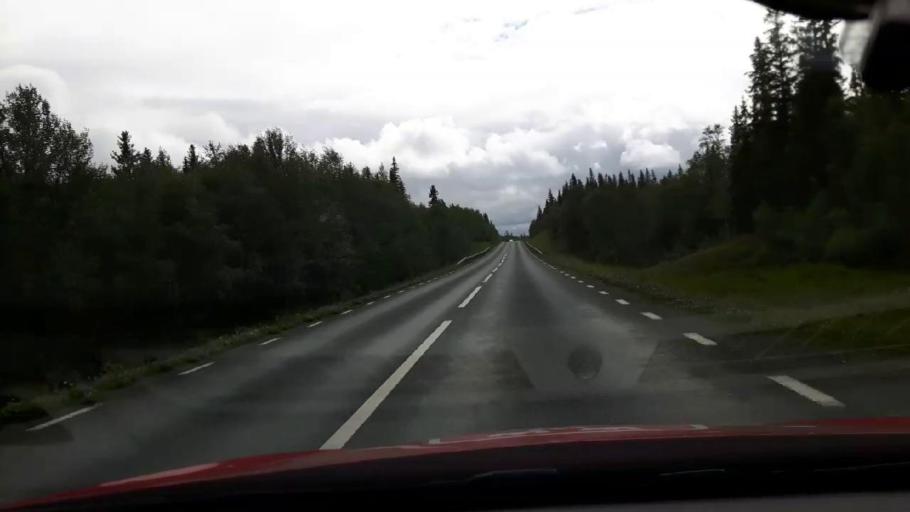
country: NO
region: Nord-Trondelag
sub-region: Meraker
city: Meraker
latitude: 63.2855
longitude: 12.3203
